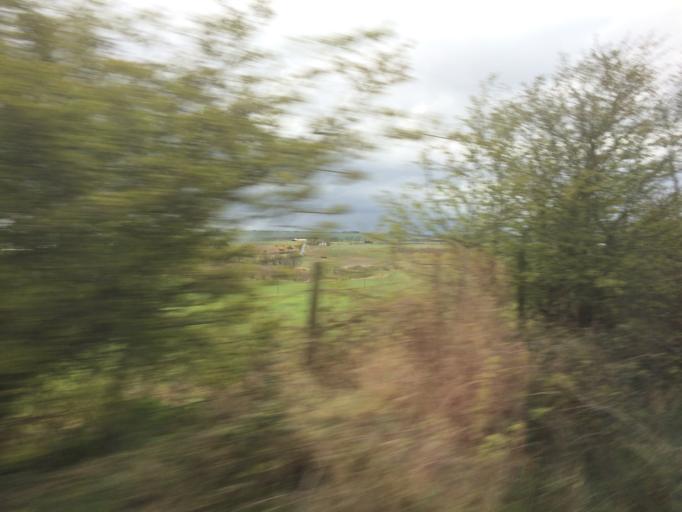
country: GB
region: Scotland
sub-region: Angus
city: Montrose
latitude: 56.6561
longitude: -2.5178
